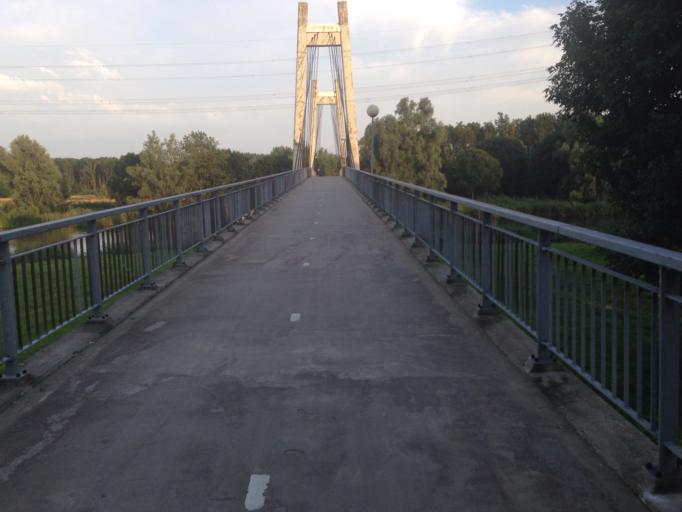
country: NL
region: Flevoland
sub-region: Gemeente Almere
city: Almere Stad
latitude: 52.3879
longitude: 5.2920
